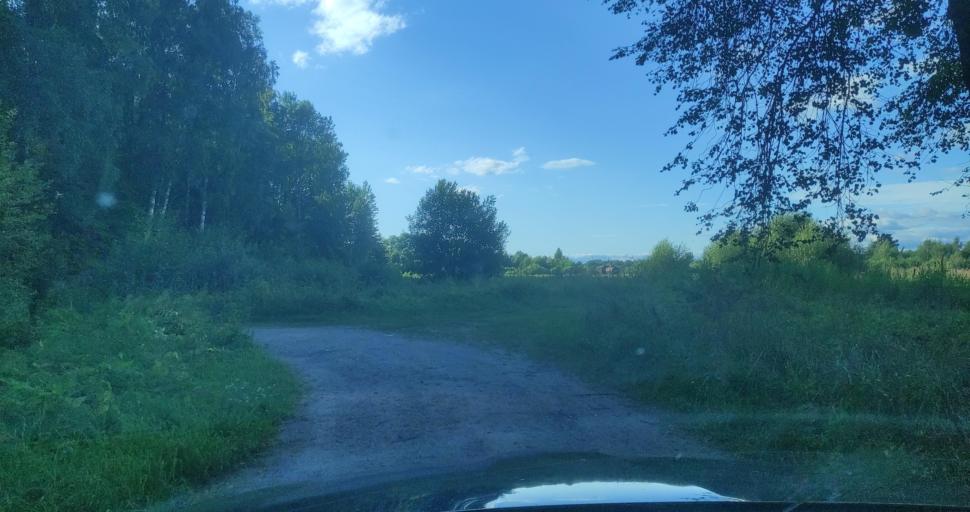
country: LV
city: Tireli
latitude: 56.7029
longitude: 23.4613
